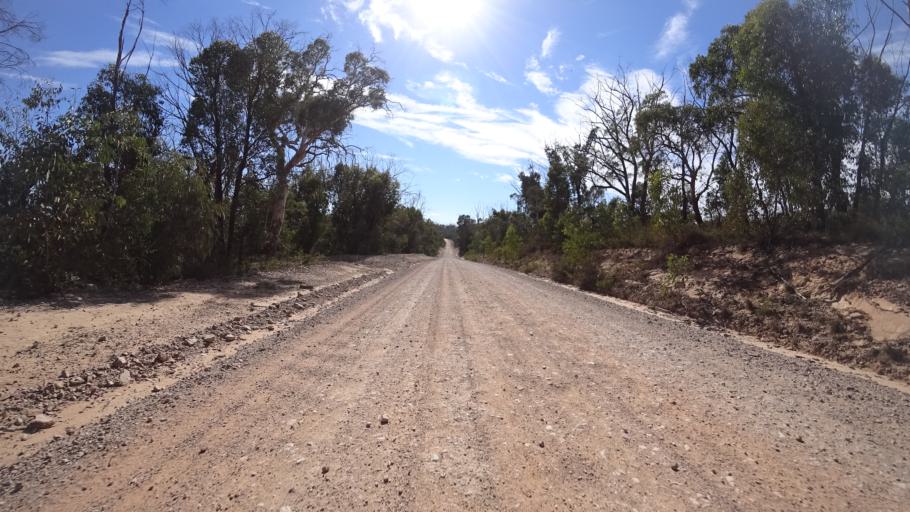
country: AU
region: New South Wales
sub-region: Lithgow
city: Lithgow
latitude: -33.4333
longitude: 150.1886
